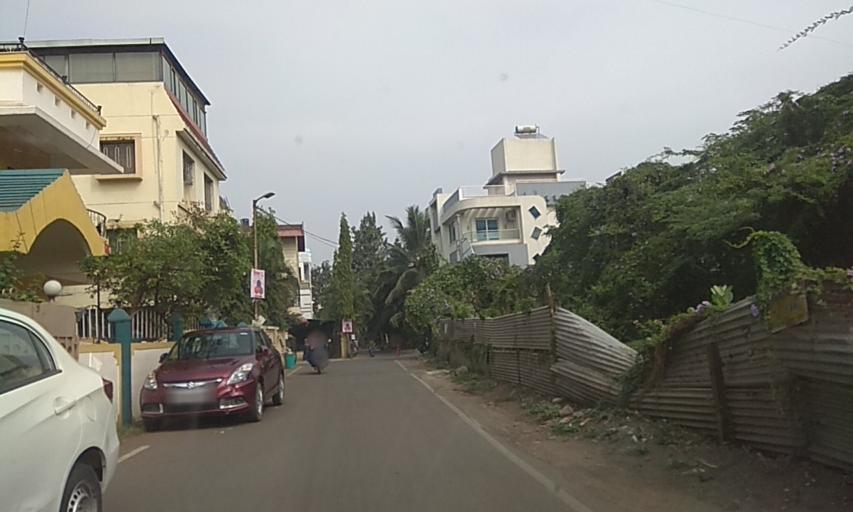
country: IN
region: Maharashtra
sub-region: Pune Division
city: Pune
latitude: 18.5038
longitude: 73.9318
